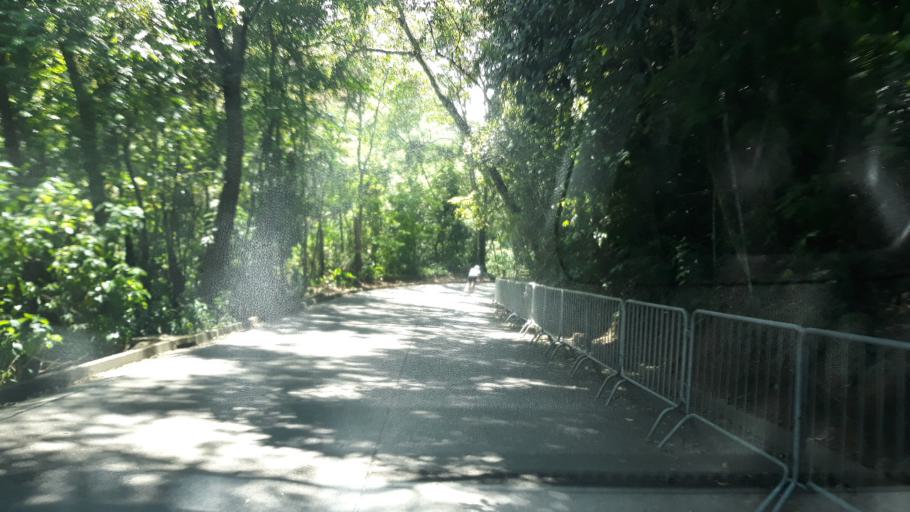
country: BR
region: Rio de Janeiro
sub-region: Rio De Janeiro
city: Rio de Janeiro
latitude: -22.9454
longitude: -43.2163
